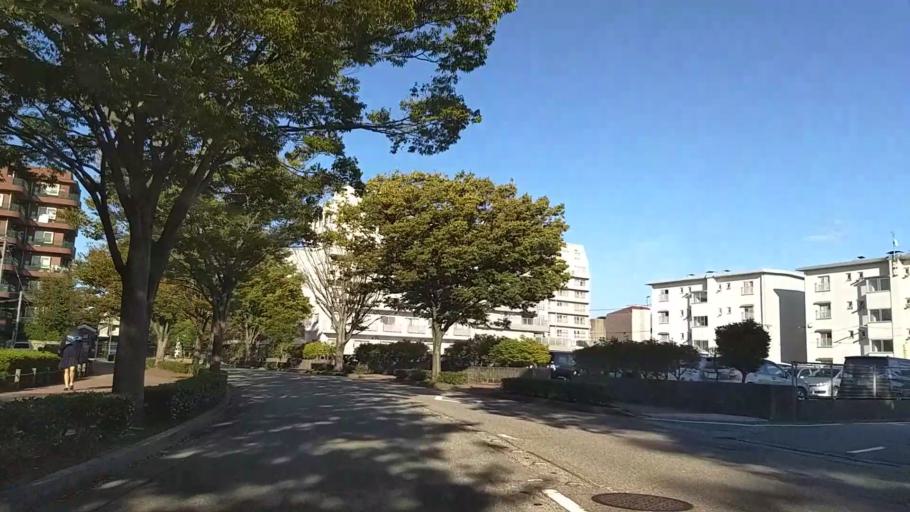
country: JP
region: Ishikawa
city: Kanazawa-shi
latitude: 36.5580
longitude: 136.6651
